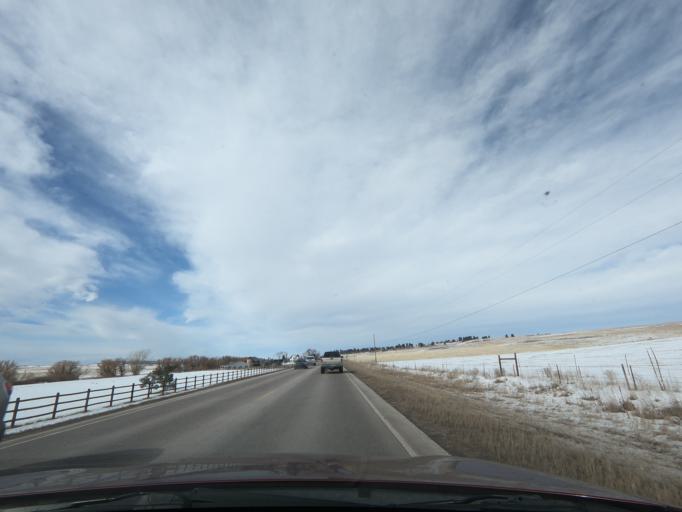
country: US
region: Colorado
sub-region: Elbert County
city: Elizabeth
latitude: 39.2411
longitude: -104.6969
